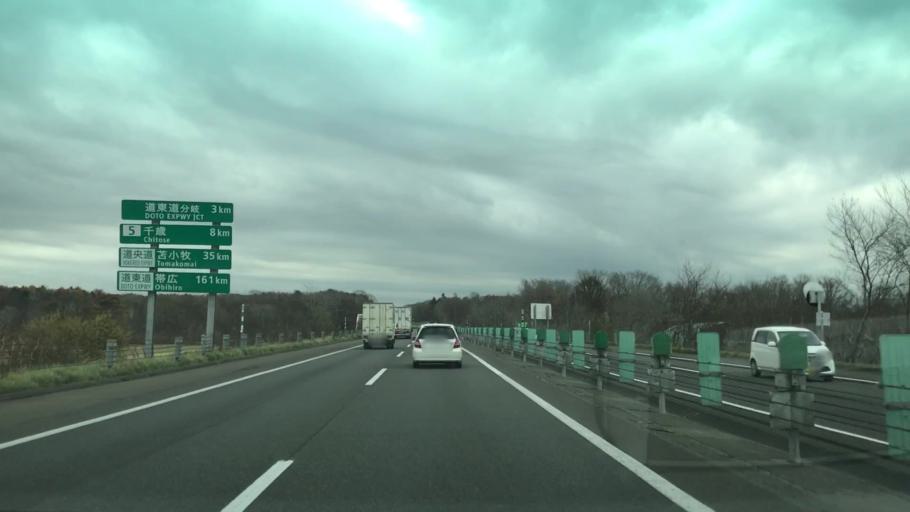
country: JP
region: Hokkaido
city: Chitose
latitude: 42.8655
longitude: 141.5571
